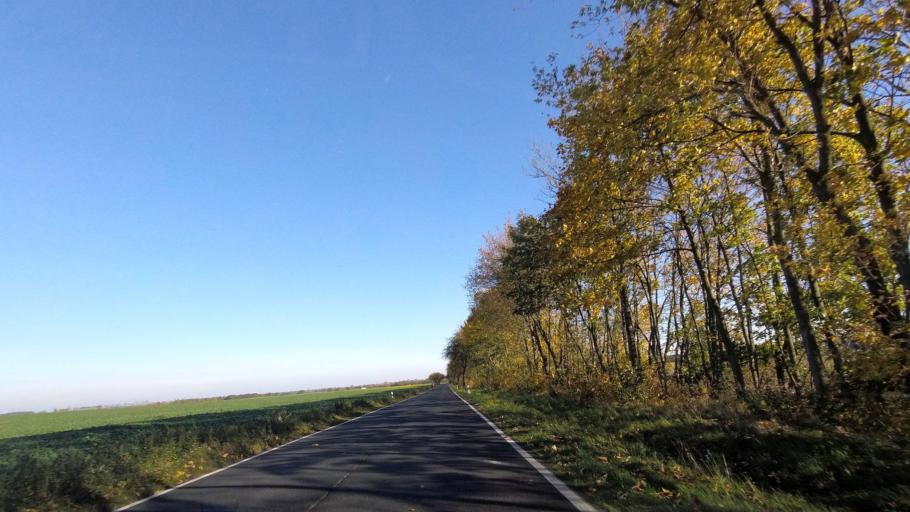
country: DE
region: Saxony-Anhalt
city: Zahna
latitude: 51.9726
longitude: 12.8452
